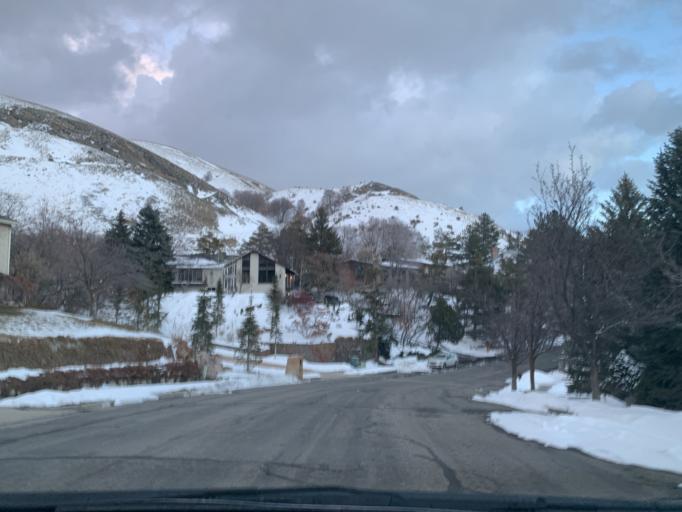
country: US
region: Utah
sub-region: Salt Lake County
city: Salt Lake City
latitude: 40.7819
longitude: -111.8435
